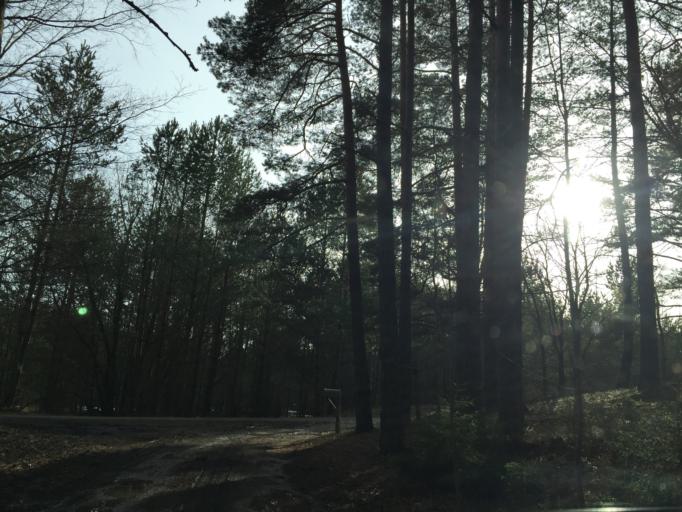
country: EE
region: Paernumaa
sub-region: Paernu linn
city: Parnu
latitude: 58.2155
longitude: 24.5060
